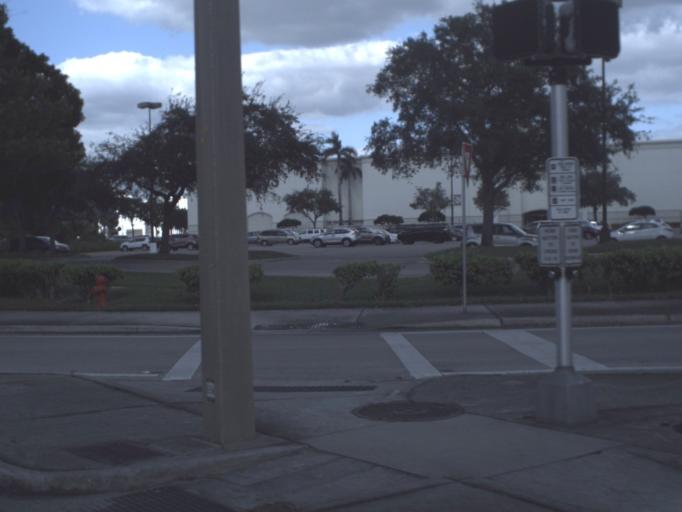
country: US
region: Florida
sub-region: Collier County
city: Naples
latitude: 26.1677
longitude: -81.7990
